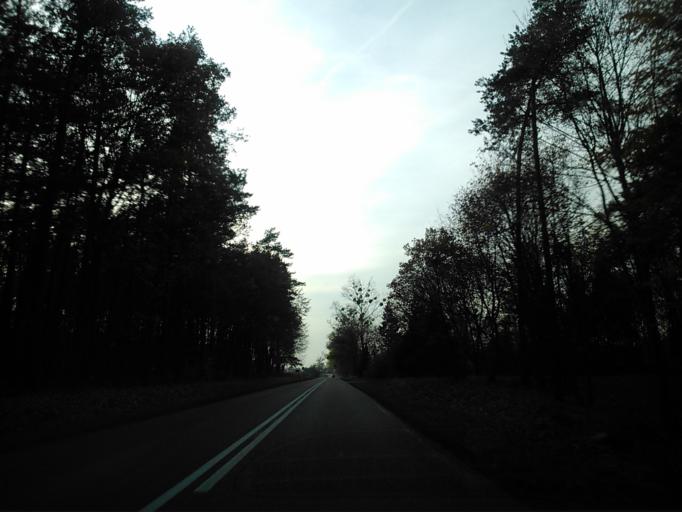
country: PL
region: Warmian-Masurian Voivodeship
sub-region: Powiat dzialdowski
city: Lidzbark
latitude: 53.2713
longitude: 19.8011
